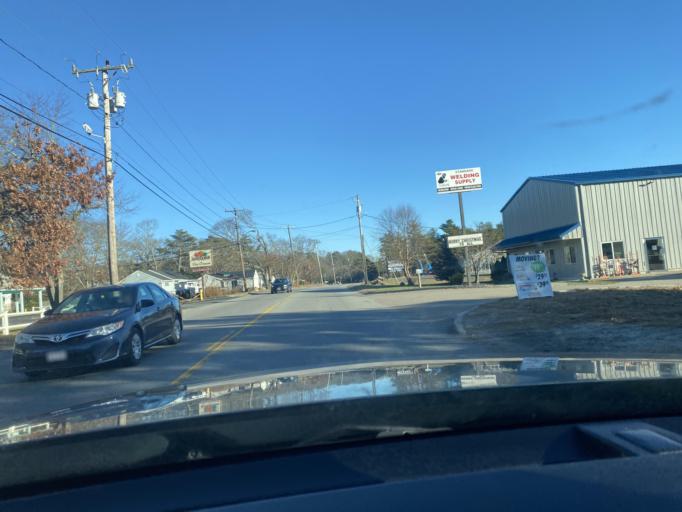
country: US
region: Massachusetts
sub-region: Plymouth County
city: Wareham Center
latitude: 41.7696
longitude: -70.7003
